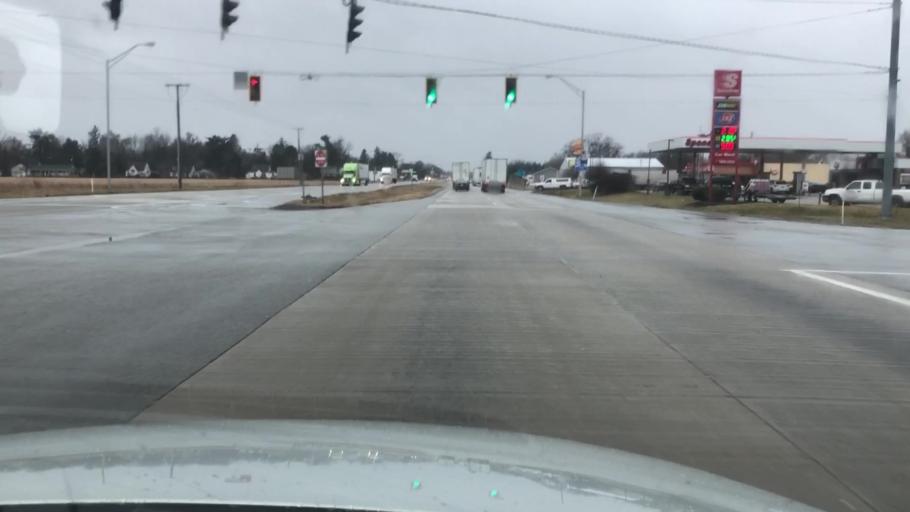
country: US
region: Indiana
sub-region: LaPorte County
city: Wanatah
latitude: 41.4341
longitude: -86.8912
